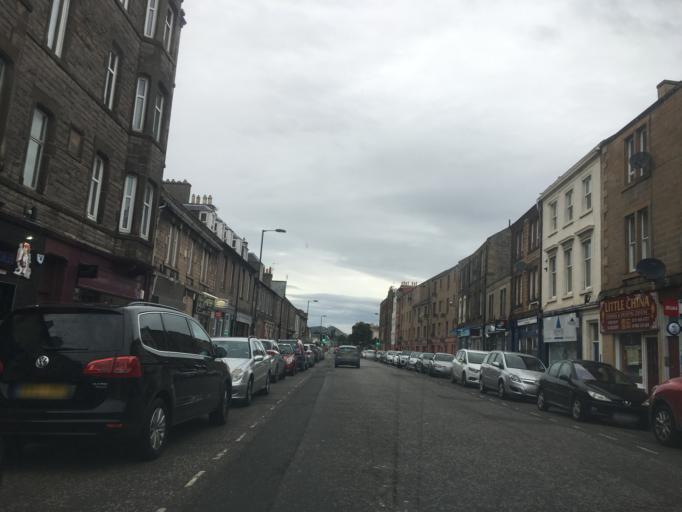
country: GB
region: Scotland
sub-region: East Lothian
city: Musselburgh
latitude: 55.9439
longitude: -3.0604
